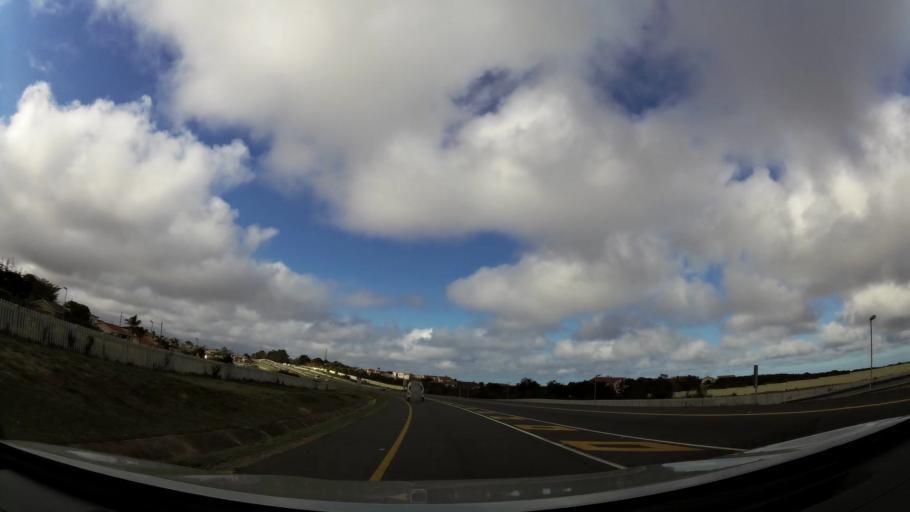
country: ZA
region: Western Cape
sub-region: Eden District Municipality
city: Plettenberg Bay
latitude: -34.0546
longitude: 23.3429
